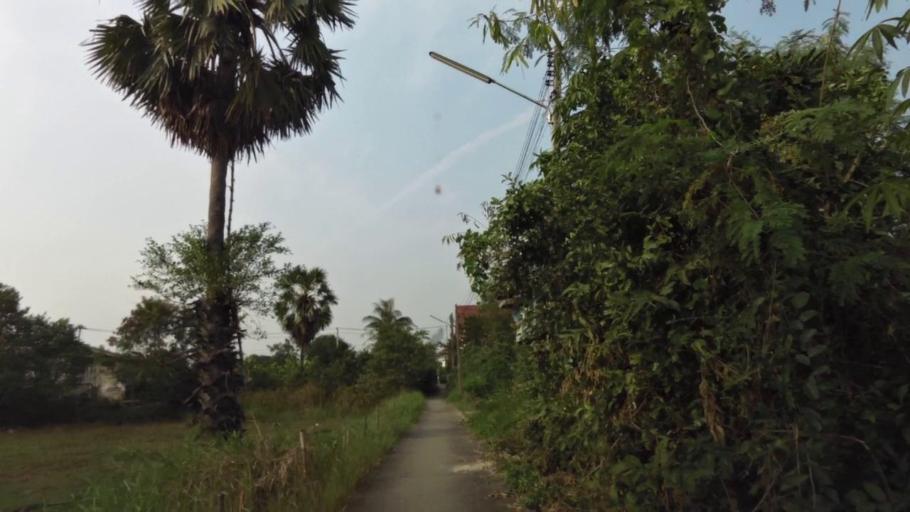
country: TH
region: Phra Nakhon Si Ayutthaya
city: Phra Nakhon Si Ayutthaya
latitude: 14.3433
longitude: 100.5693
